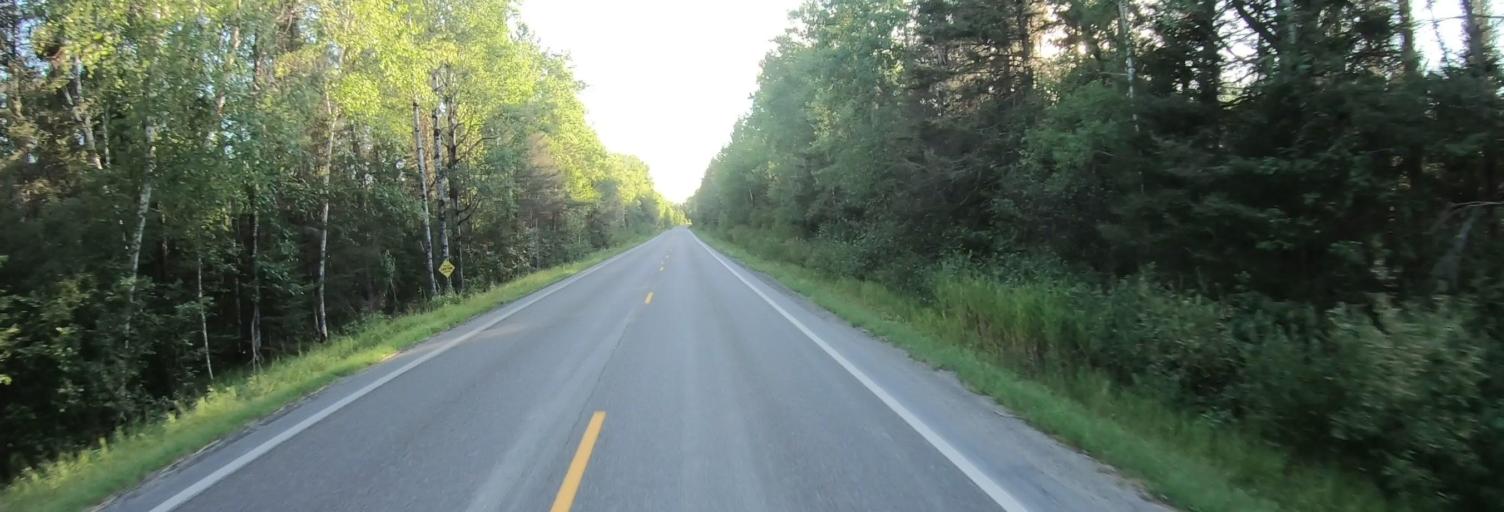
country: US
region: Minnesota
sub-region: Saint Louis County
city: Ely
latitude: 47.9332
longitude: -91.7020
